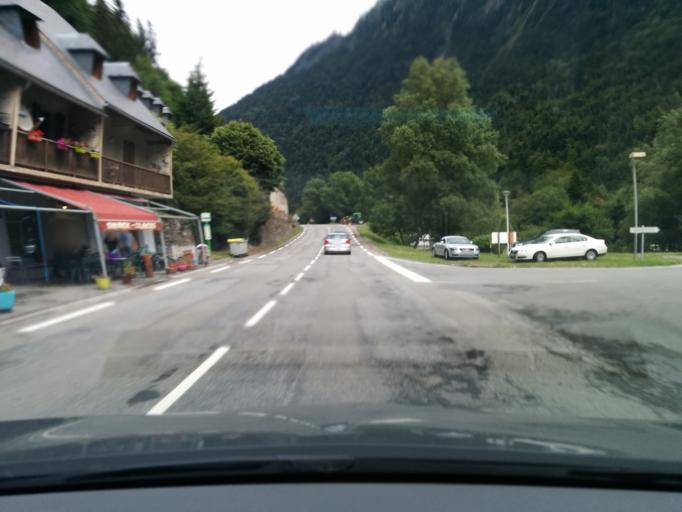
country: FR
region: Midi-Pyrenees
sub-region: Departement des Hautes-Pyrenees
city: Saint-Lary-Soulan
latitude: 42.7870
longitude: 0.2467
